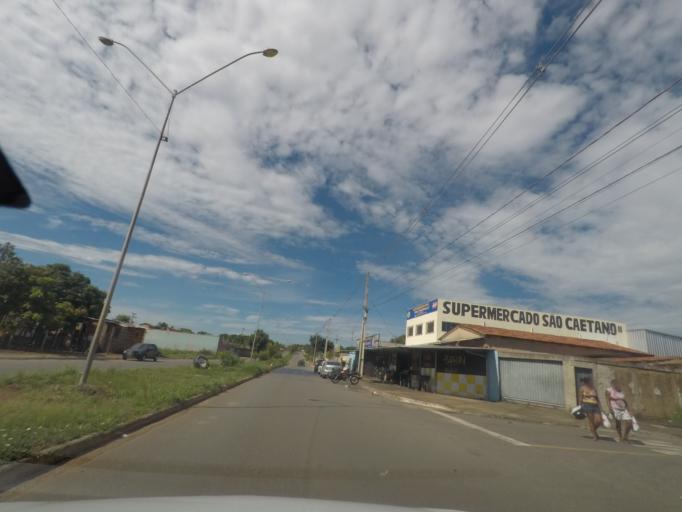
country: BR
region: Goias
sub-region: Aparecida De Goiania
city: Aparecida de Goiania
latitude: -16.8157
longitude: -49.2892
